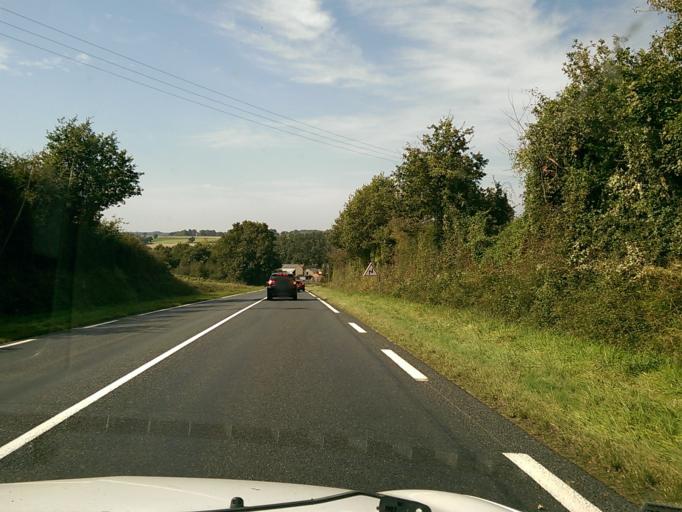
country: FR
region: Pays de la Loire
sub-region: Departement de Maine-et-Loire
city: Nueil-sur-Layon
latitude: 47.1529
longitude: -0.4370
